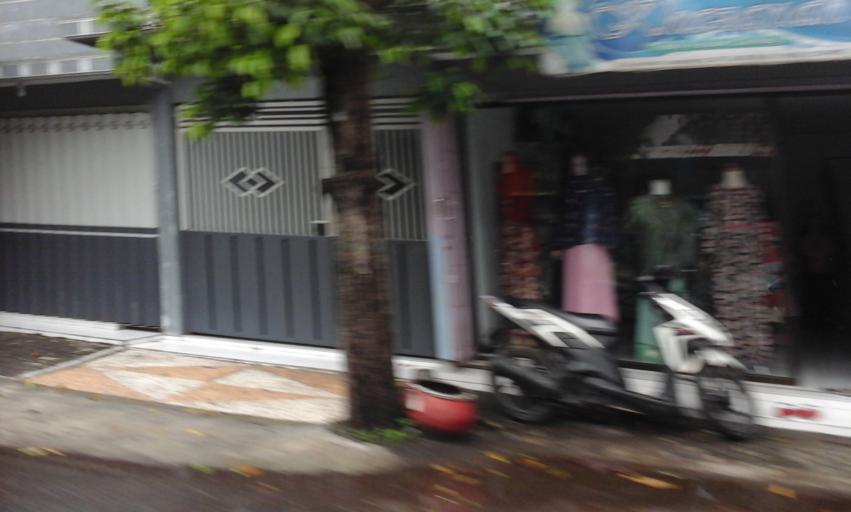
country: ID
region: East Java
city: Kadipaten
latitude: -8.1333
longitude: 113.2198
